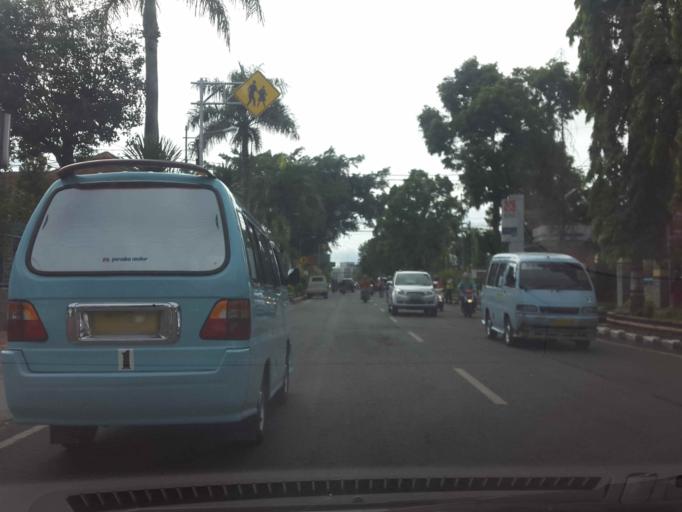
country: ID
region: Central Java
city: Salatiga
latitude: -7.3234
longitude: 110.5026
